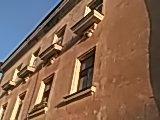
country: RU
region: Orenburg
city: Novotroitsk
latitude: 51.2056
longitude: 58.2994
